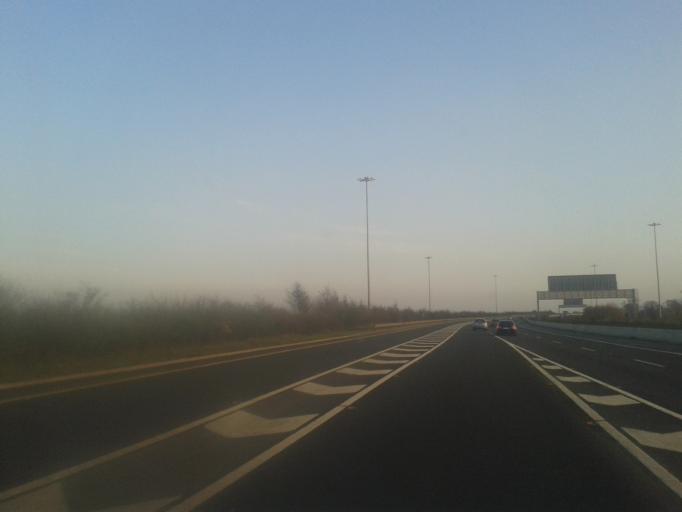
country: IE
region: Leinster
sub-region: Fingal County
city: Swords
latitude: 53.4749
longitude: -6.2033
